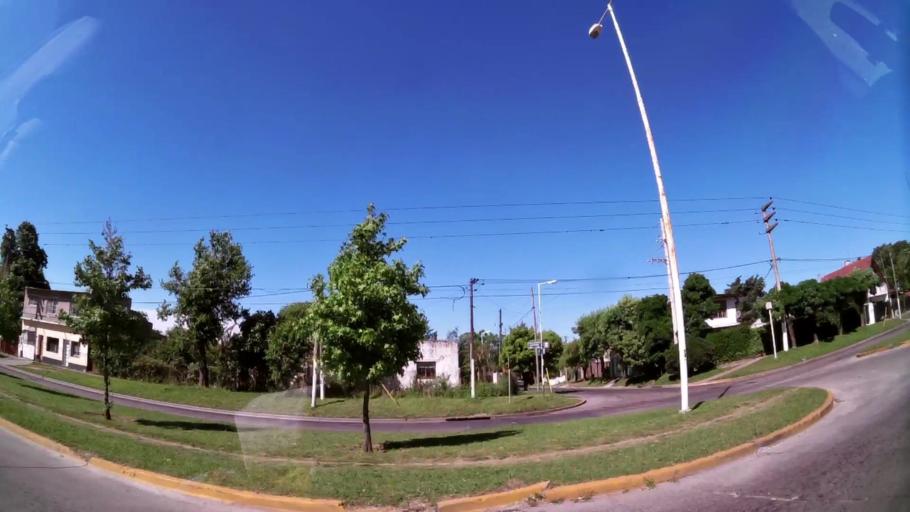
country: AR
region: Buenos Aires
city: Santa Catalina - Dique Lujan
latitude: -34.4932
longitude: -58.6971
